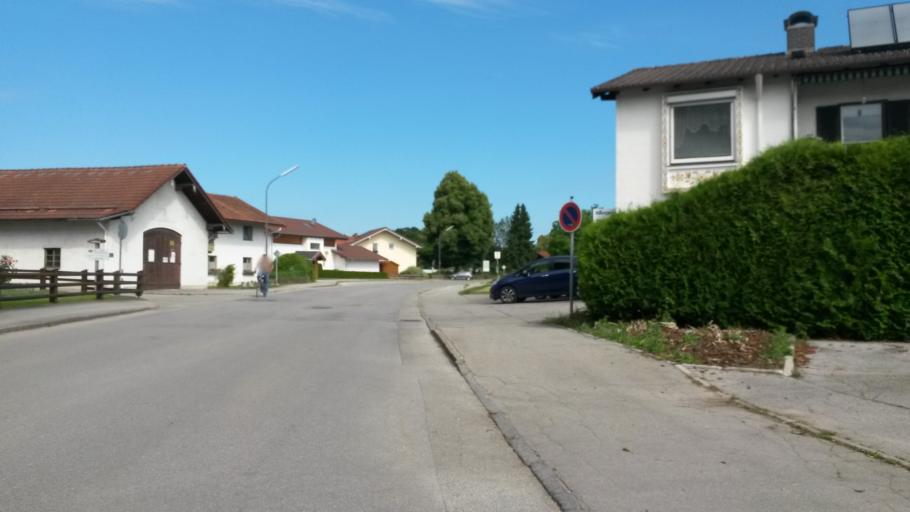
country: DE
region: Bavaria
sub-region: Upper Bavaria
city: Ubersee
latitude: 47.8277
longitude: 12.4822
